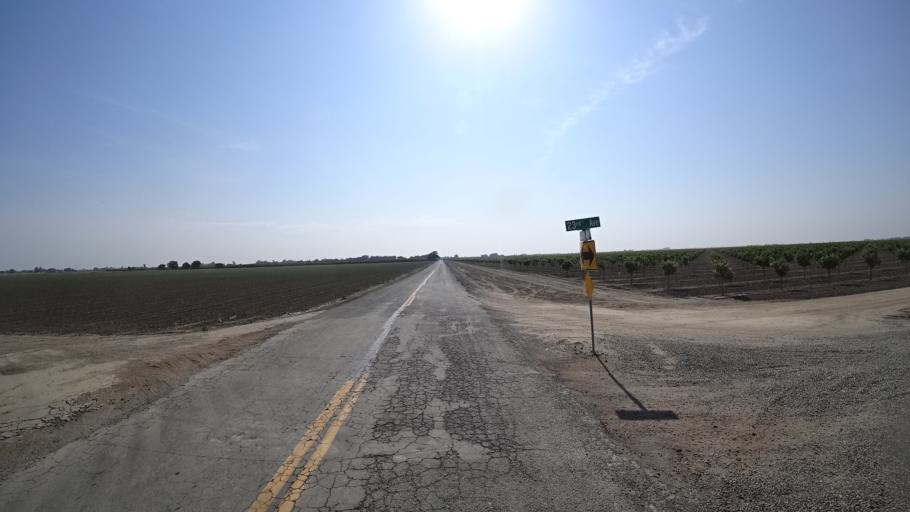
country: US
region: California
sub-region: Kings County
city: Lemoore Station
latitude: 36.3286
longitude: -119.8694
